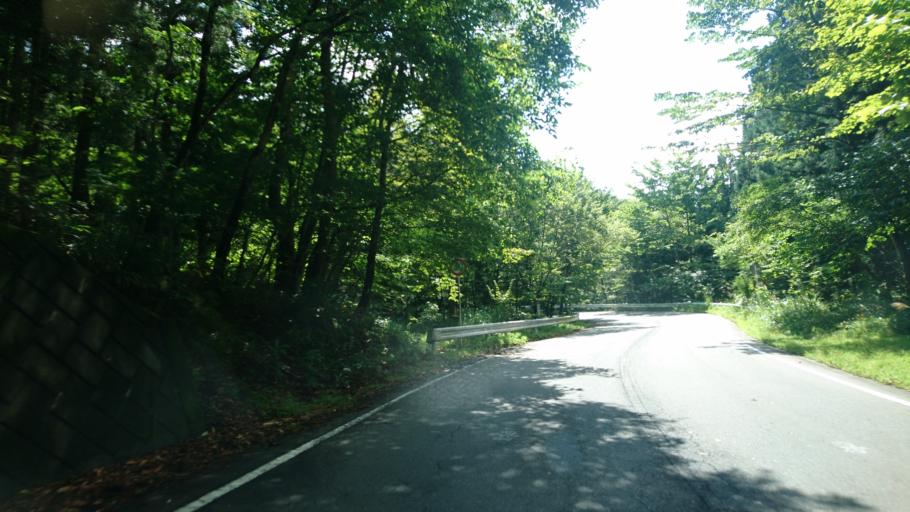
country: JP
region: Gunma
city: Omamacho-omama
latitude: 36.5698
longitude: 139.2390
